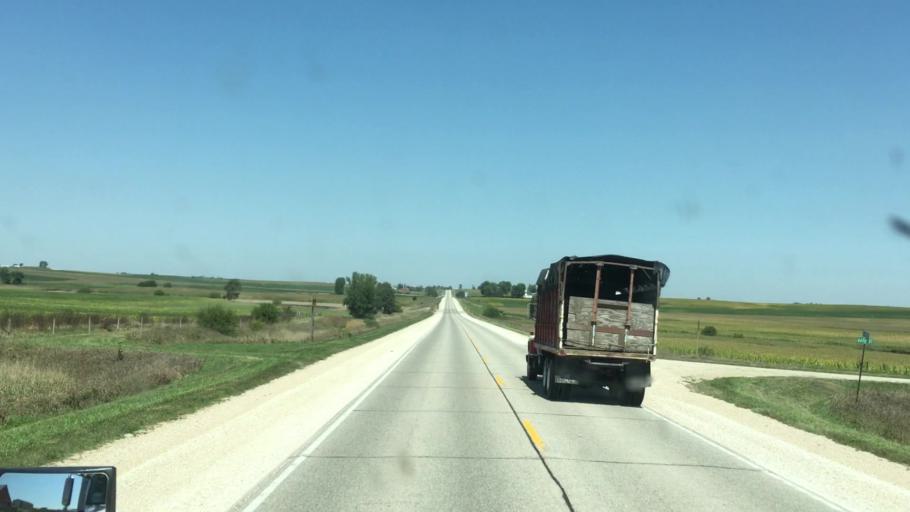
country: US
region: Iowa
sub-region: Tama County
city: Dysart
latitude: 42.0647
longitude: -92.2989
